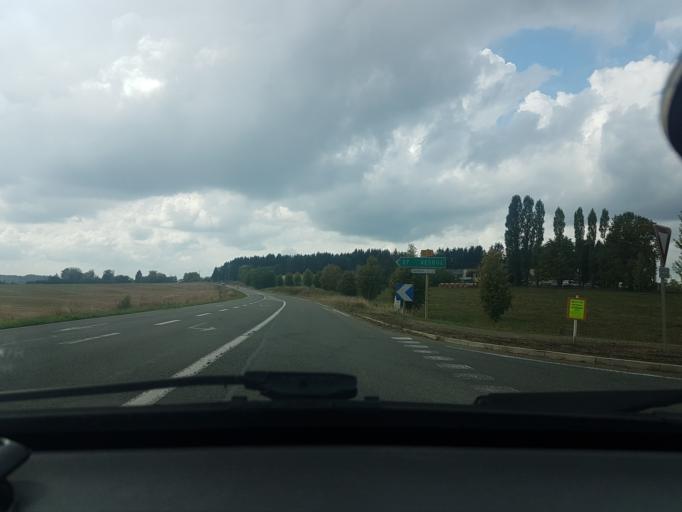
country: FR
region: Franche-Comte
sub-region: Departement de la Haute-Saone
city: Villersexel
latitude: 47.5491
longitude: 6.4452
